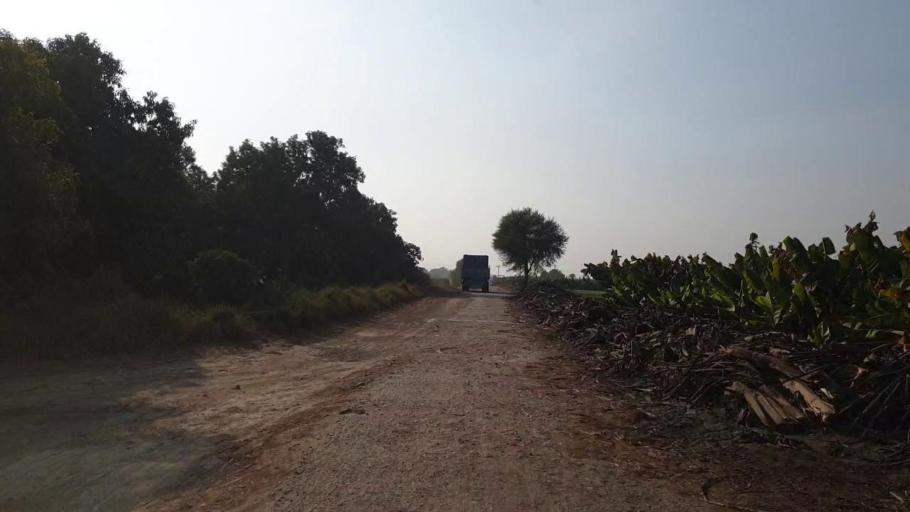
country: PK
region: Sindh
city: Matiari
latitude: 25.5995
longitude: 68.6103
